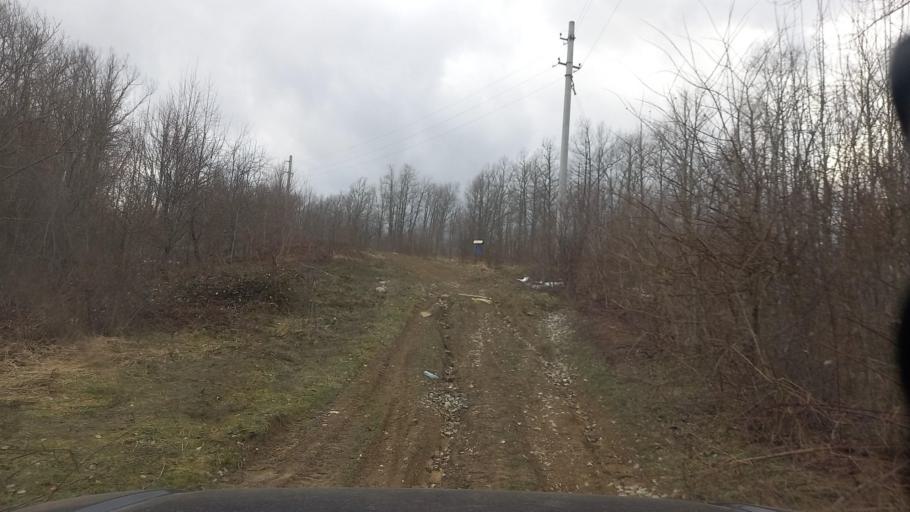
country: RU
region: Krasnodarskiy
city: Smolenskaya
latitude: 44.5706
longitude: 38.7929
